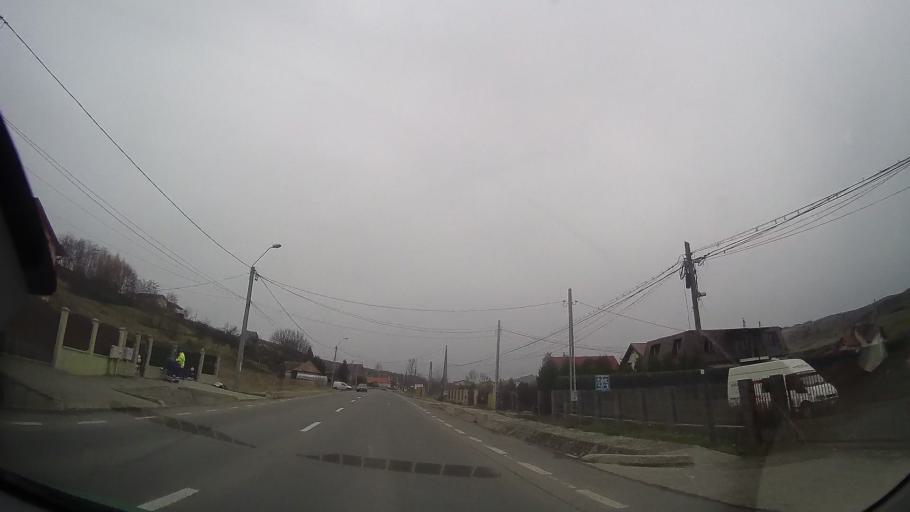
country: RO
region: Mures
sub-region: Comuna Ceausu de Campie
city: Ceausu de Campie
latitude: 46.6043
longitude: 24.5301
